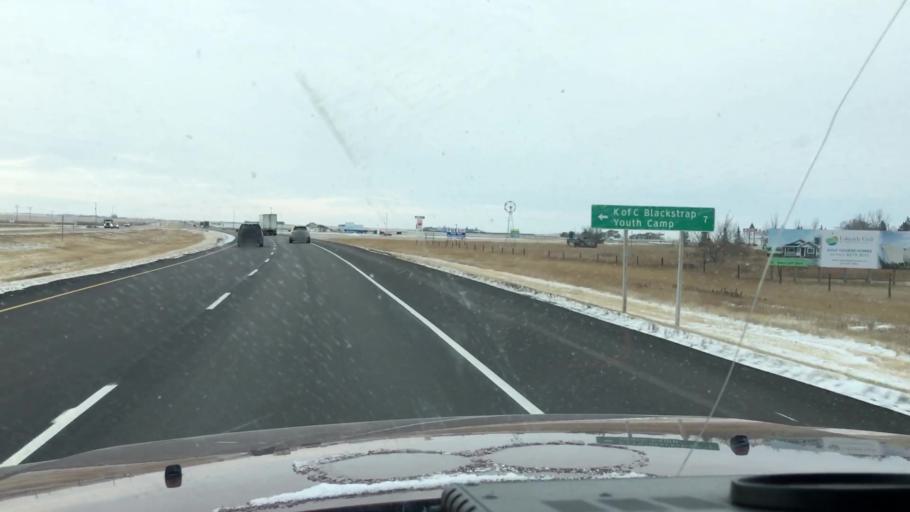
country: CA
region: Saskatchewan
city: Saskatoon
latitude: 51.8131
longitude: -106.4975
